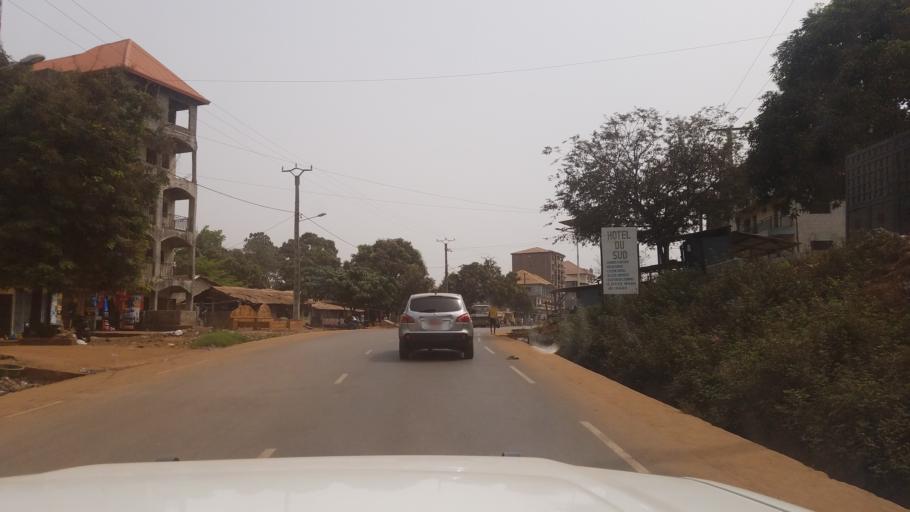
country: GN
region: Kindia
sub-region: Prefecture de Dubreka
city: Dubreka
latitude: 9.6688
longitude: -13.5905
